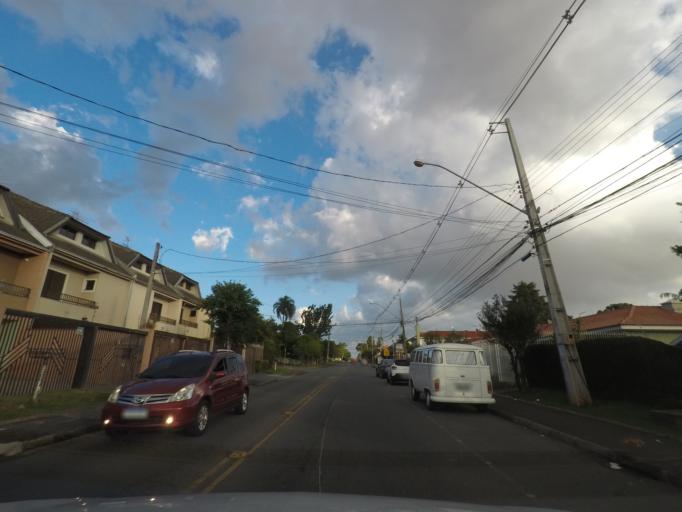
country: BR
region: Parana
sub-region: Sao Jose Dos Pinhais
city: Sao Jose dos Pinhais
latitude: -25.5066
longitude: -49.2550
